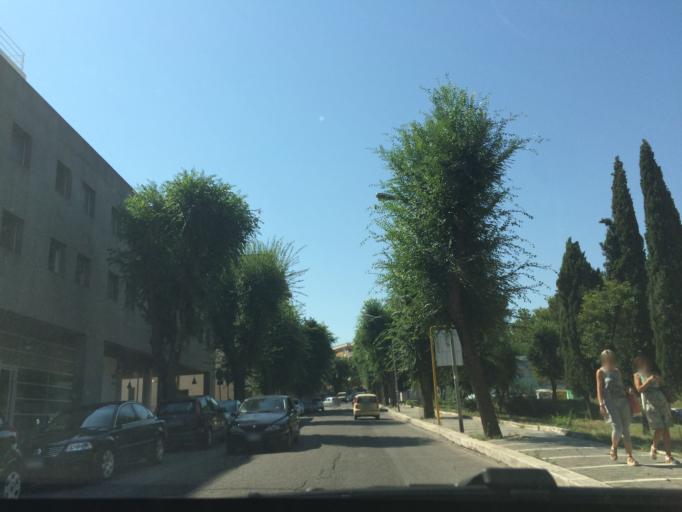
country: IT
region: Basilicate
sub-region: Provincia di Matera
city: Matera
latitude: 40.6738
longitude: 16.5988
